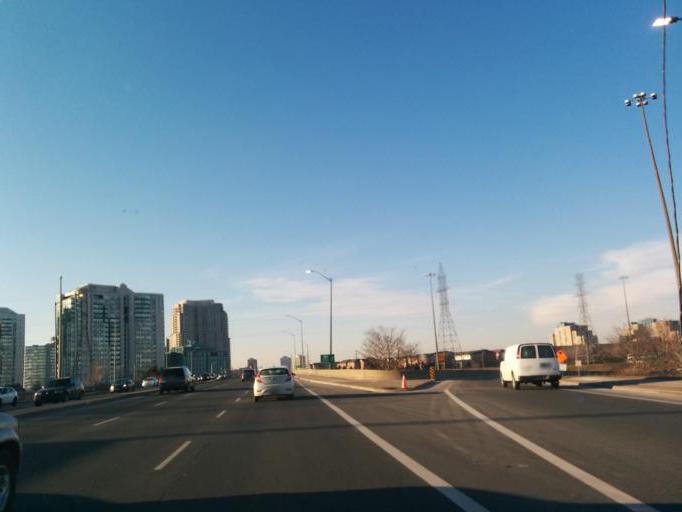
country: CA
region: Ontario
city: Mississauga
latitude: 43.5999
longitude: -79.6433
